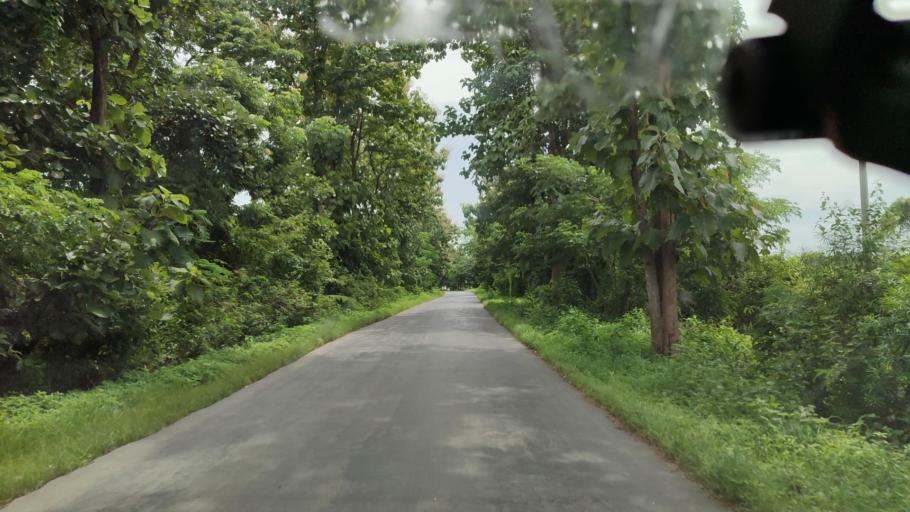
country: MM
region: Bago
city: Pyay
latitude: 18.7101
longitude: 95.0026
